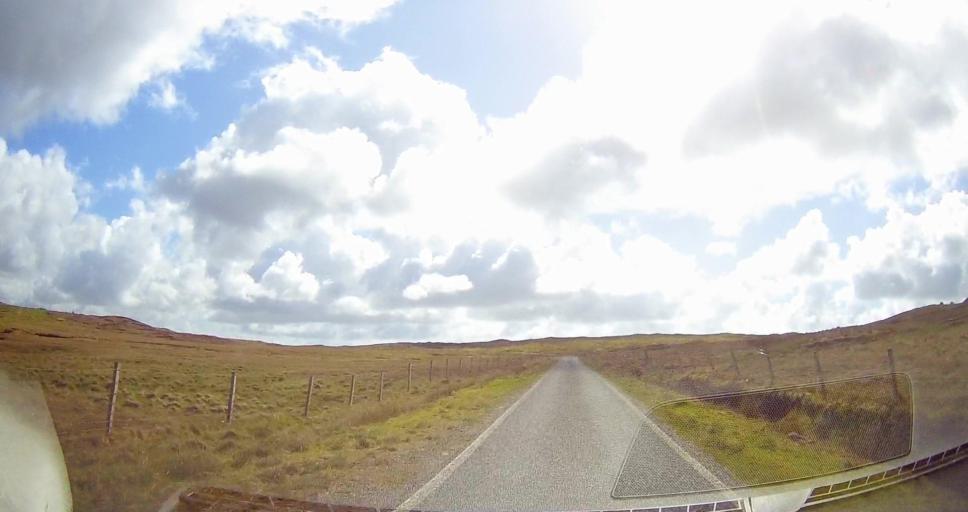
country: GB
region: Scotland
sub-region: Shetland Islands
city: Lerwick
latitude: 60.5024
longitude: -1.3948
